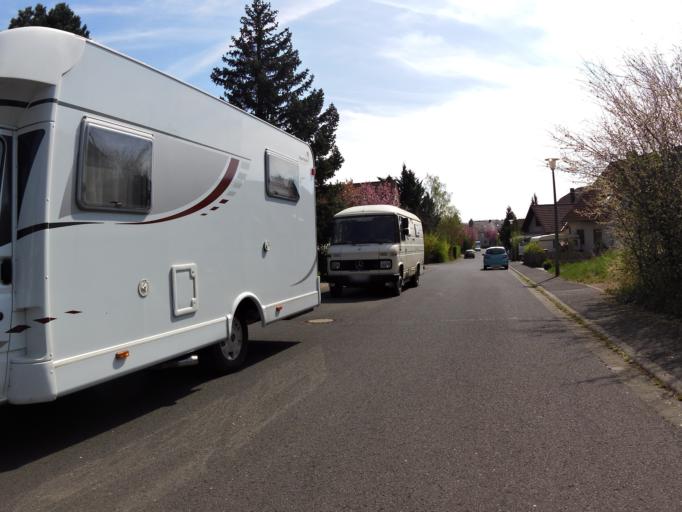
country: DE
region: Bavaria
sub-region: Regierungsbezirk Unterfranken
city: Unterpleichfeld
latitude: 49.8713
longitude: 10.0440
